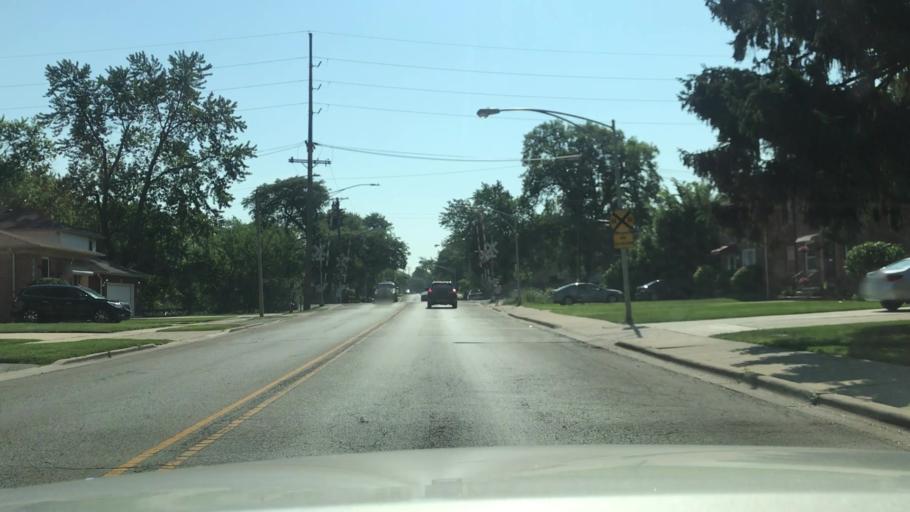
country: US
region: Illinois
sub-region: Cook County
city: Evergreen Park
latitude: 41.7136
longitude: -87.6878
